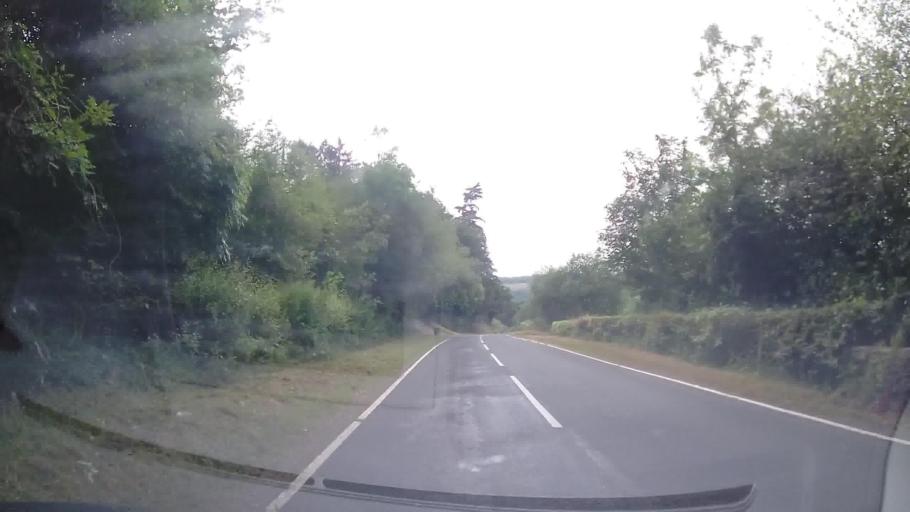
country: GB
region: Wales
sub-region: Denbighshire
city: Llandrillo
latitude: 52.9165
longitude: -3.4994
